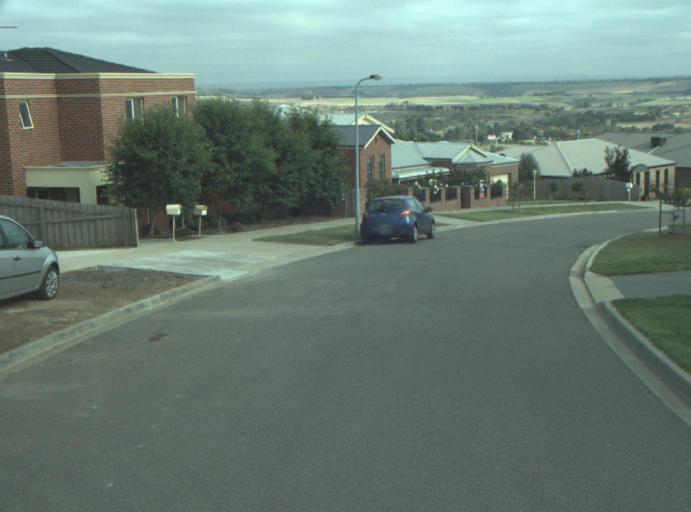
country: AU
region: Victoria
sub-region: Greater Geelong
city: Wandana Heights
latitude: -38.1549
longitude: 144.3117
